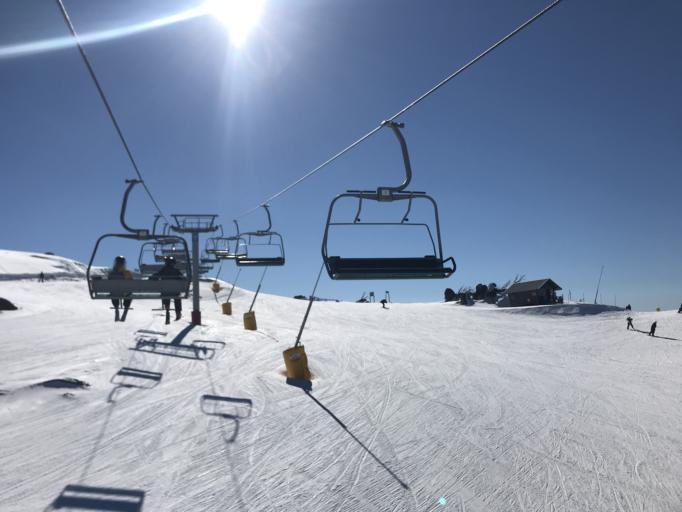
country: AU
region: New South Wales
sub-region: Snowy River
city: Jindabyne
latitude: -36.3782
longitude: 148.3955
